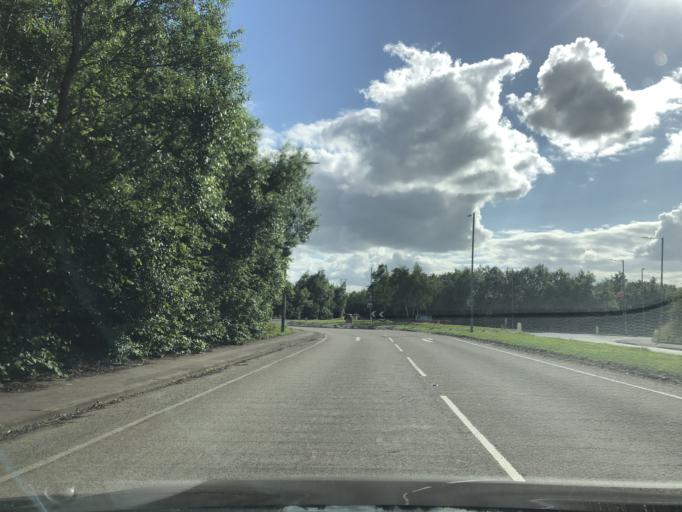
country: GB
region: Northern Ireland
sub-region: Ards District
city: Comber
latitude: 54.5518
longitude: -5.7286
